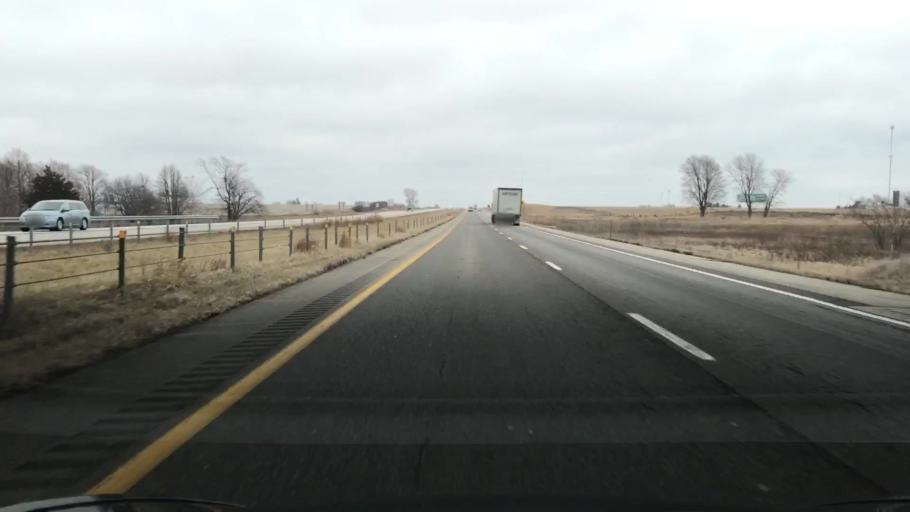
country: US
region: Iowa
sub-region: Guthrie County
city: Stuart
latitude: 41.4929
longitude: -94.3184
